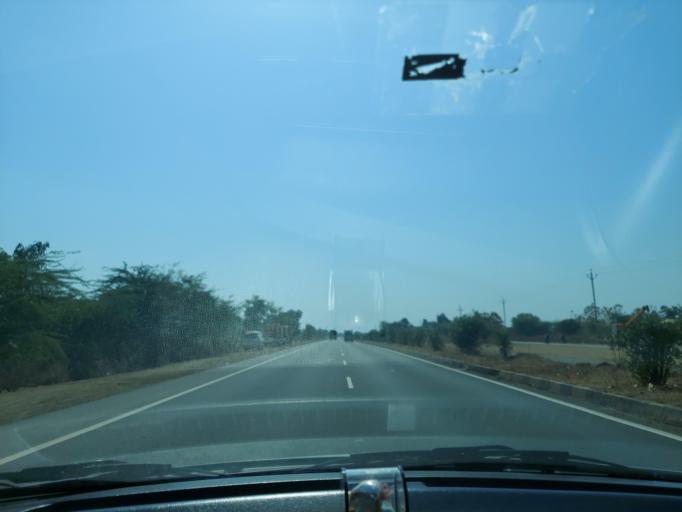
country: IN
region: Madhya Pradesh
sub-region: Dhar
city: Dhamnod
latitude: 22.3062
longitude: 75.5028
